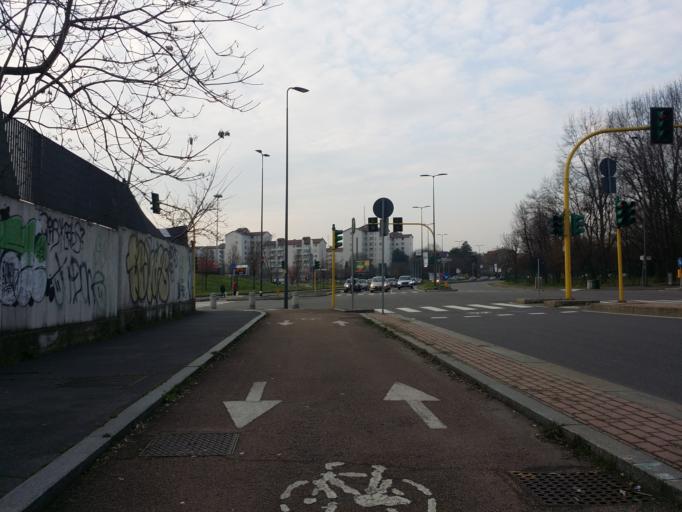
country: IT
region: Lombardy
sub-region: Citta metropolitana di Milano
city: Romano Banco
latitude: 45.4534
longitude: 9.1160
